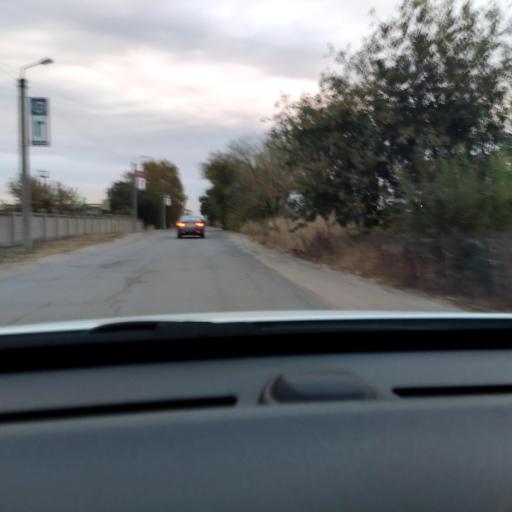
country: RU
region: Voronezj
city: Somovo
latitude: 51.6690
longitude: 39.2954
